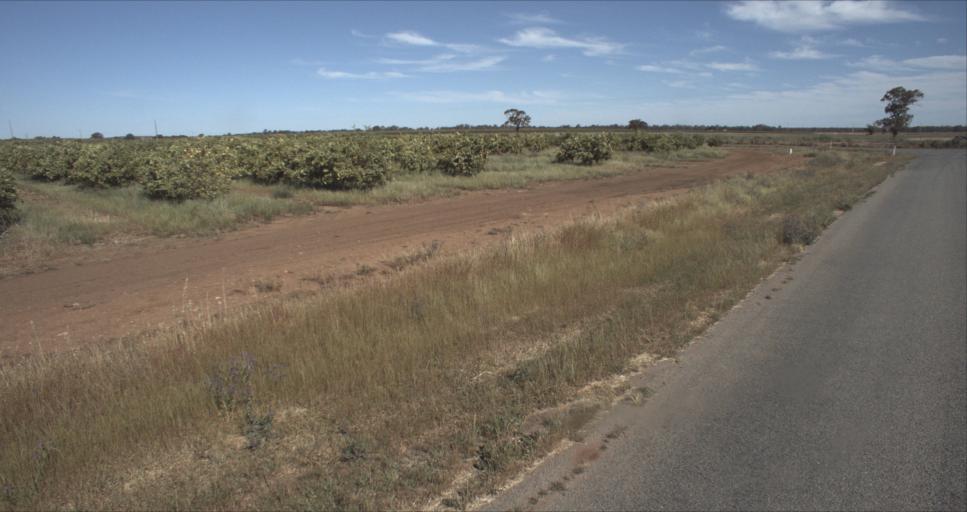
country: AU
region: New South Wales
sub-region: Leeton
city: Leeton
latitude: -34.5871
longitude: 146.3787
